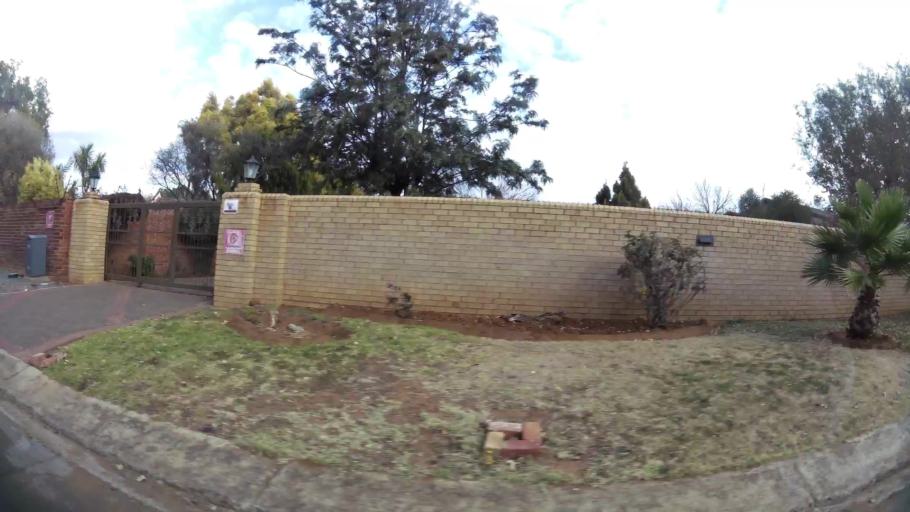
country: ZA
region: Orange Free State
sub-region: Mangaung Metropolitan Municipality
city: Bloemfontein
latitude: -29.0781
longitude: 26.1993
